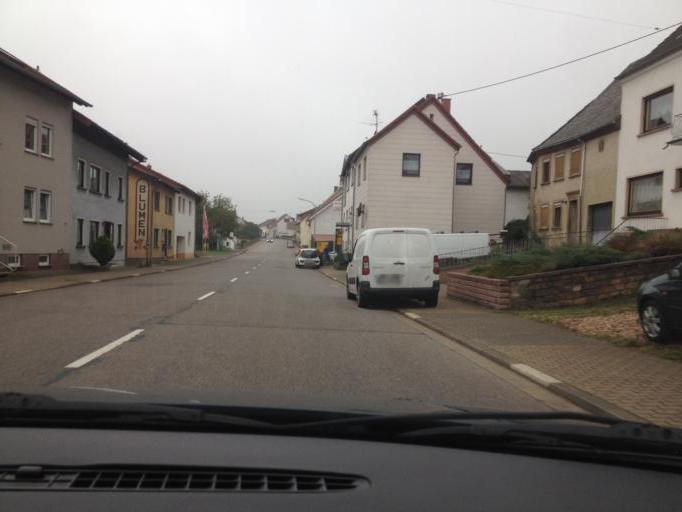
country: DE
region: Saarland
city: Tholey
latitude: 49.4628
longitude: 6.9962
